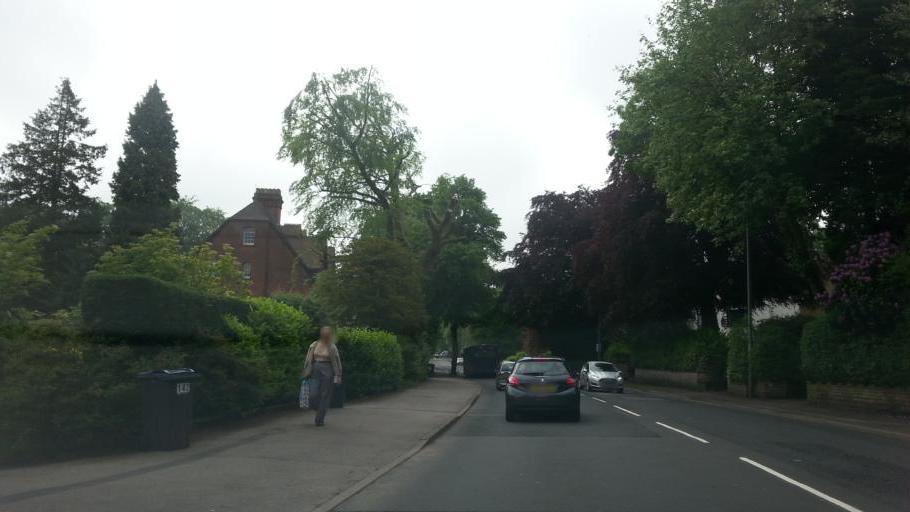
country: GB
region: England
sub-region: City and Borough of Birmingham
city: Sutton Coldfield
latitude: 52.5772
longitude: -1.8288
